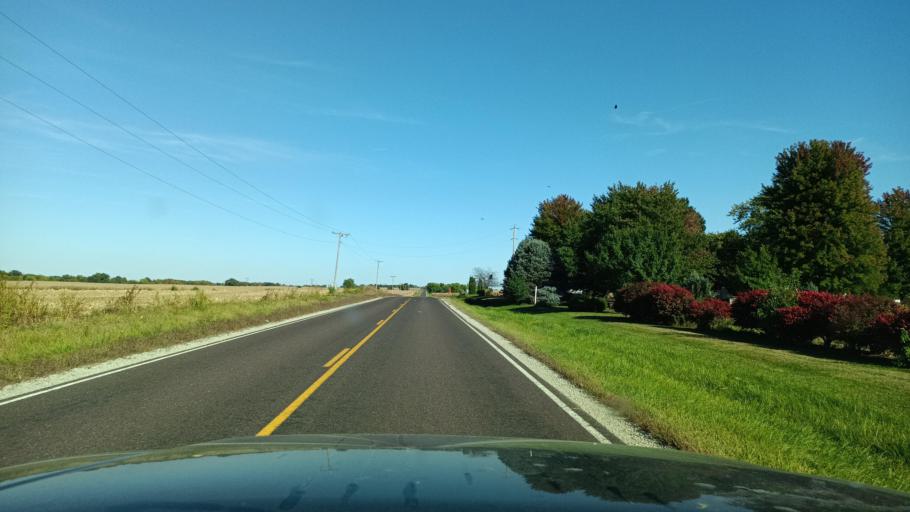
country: US
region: Illinois
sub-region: Logan County
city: Atlanta
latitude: 40.2386
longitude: -89.1094
